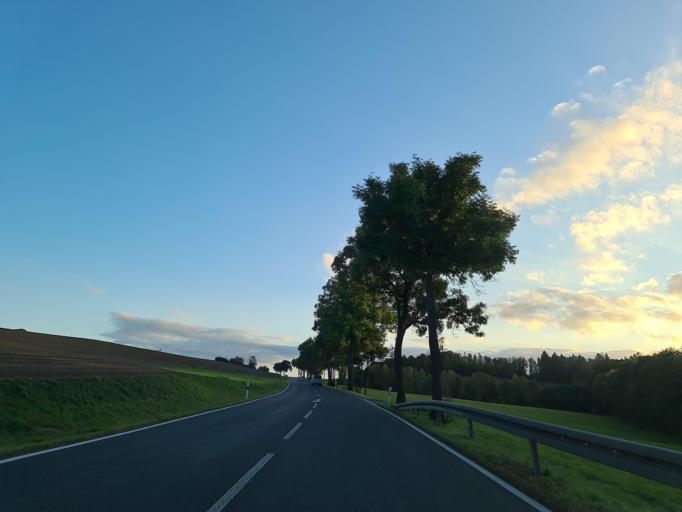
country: DE
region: Saxony
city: Syrau
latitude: 50.5695
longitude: 12.1260
